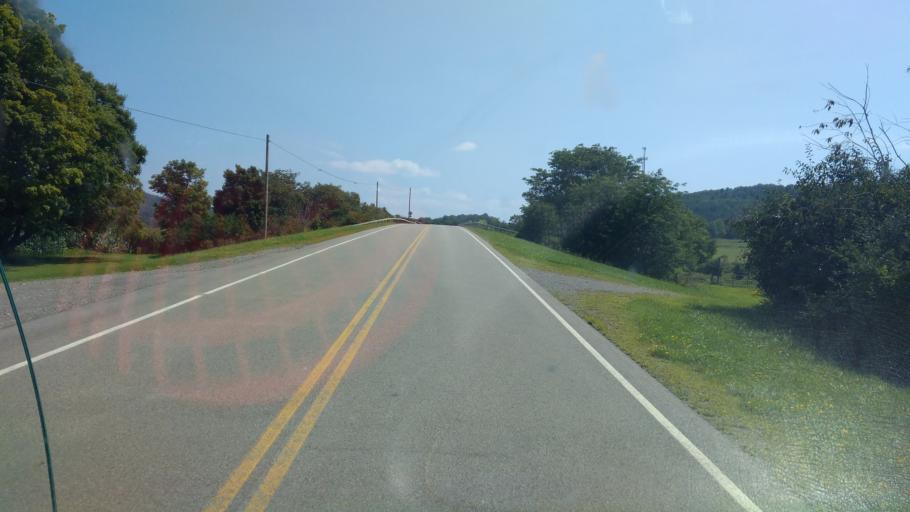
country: US
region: New York
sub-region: Allegany County
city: Belmont
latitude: 42.3000
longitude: -77.9619
